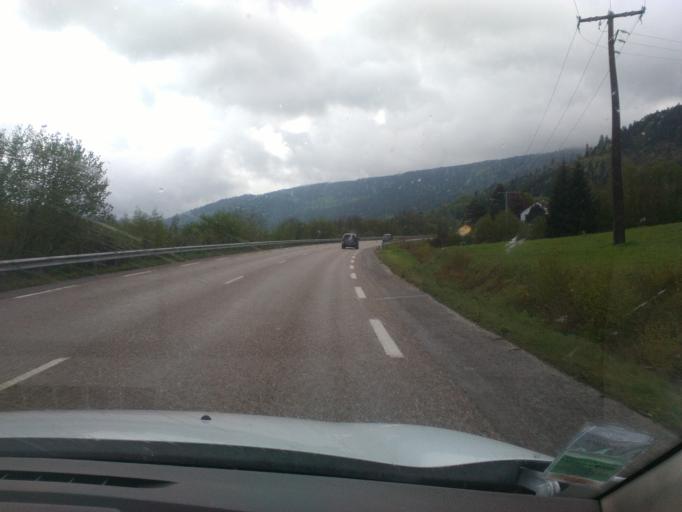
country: FR
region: Lorraine
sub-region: Departement des Vosges
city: Saulxures-sur-Moselotte
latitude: 47.9494
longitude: 6.7516
